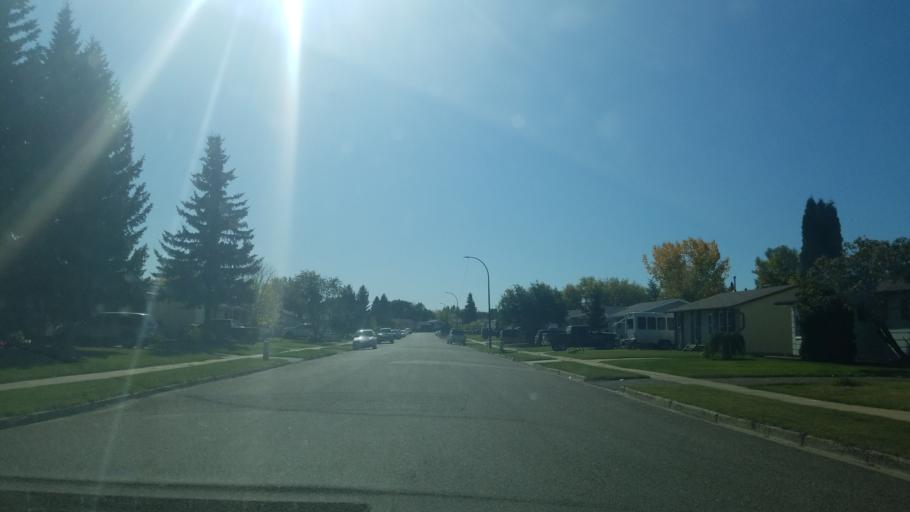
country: CA
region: Saskatchewan
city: Lloydminster
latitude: 53.2703
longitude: -110.0021
